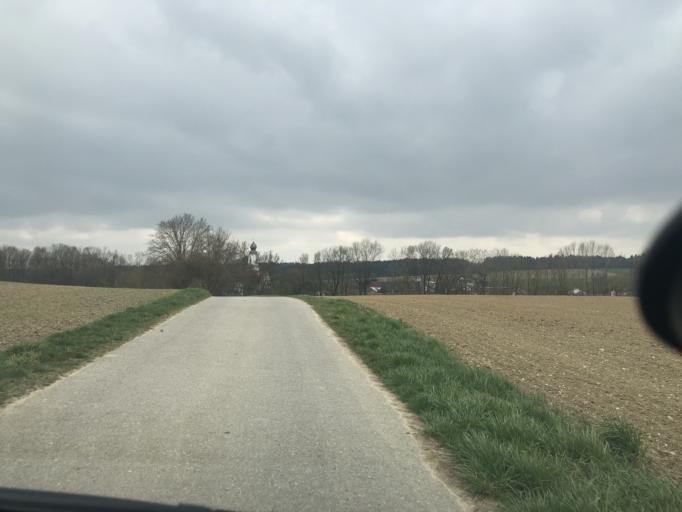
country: DE
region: Bavaria
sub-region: Upper Bavaria
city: Zolling
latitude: 48.4331
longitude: 11.7503
